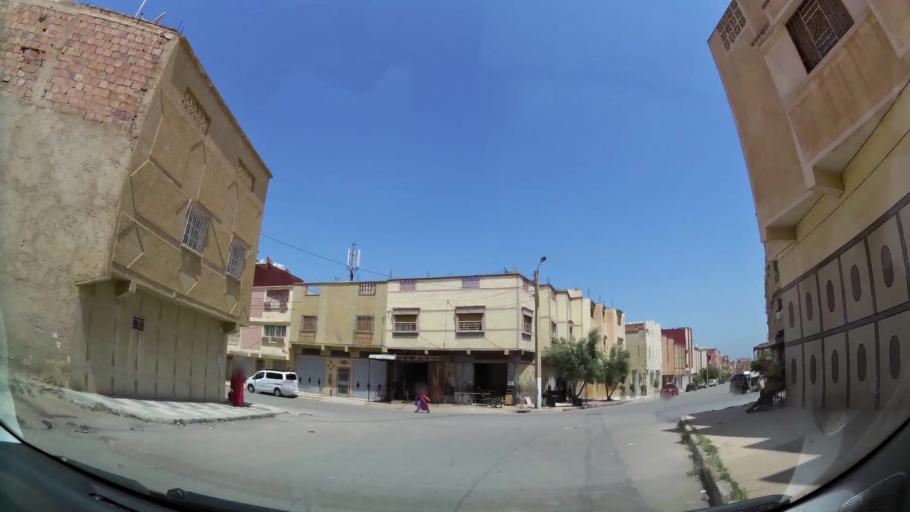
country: MA
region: Oriental
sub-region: Oujda-Angad
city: Oujda
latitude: 34.6834
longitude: -1.8889
